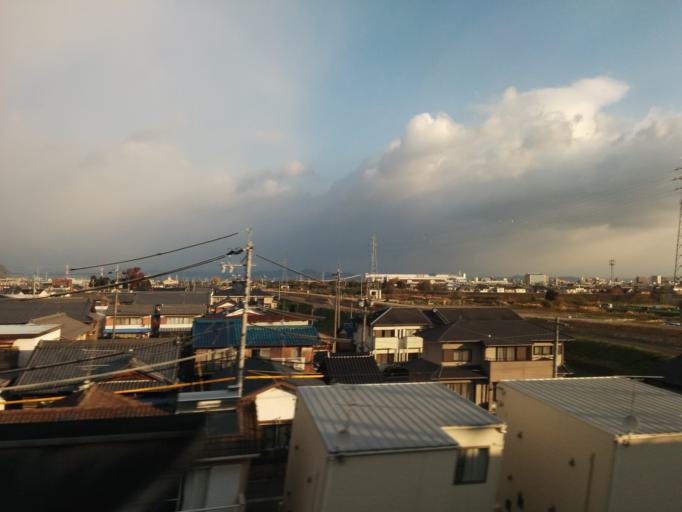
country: JP
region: Gifu
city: Ogaki
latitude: 35.3486
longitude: 136.5942
